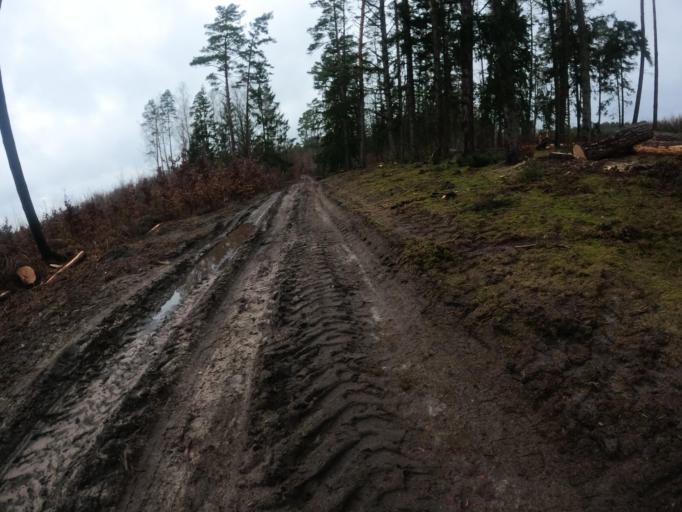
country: PL
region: West Pomeranian Voivodeship
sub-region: Powiat koszalinski
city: Polanow
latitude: 54.2407
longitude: 16.6927
